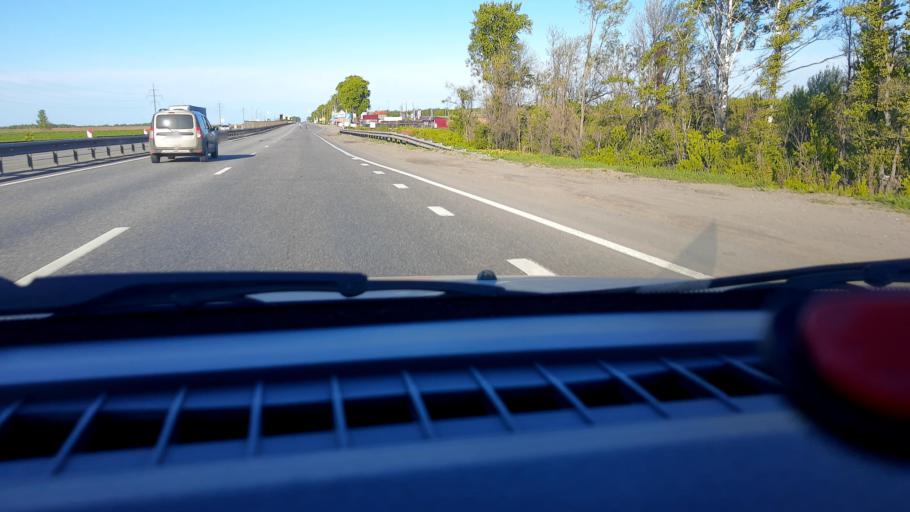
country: RU
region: Vladimir
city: Gorokhovets
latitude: 56.1690
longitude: 42.6328
